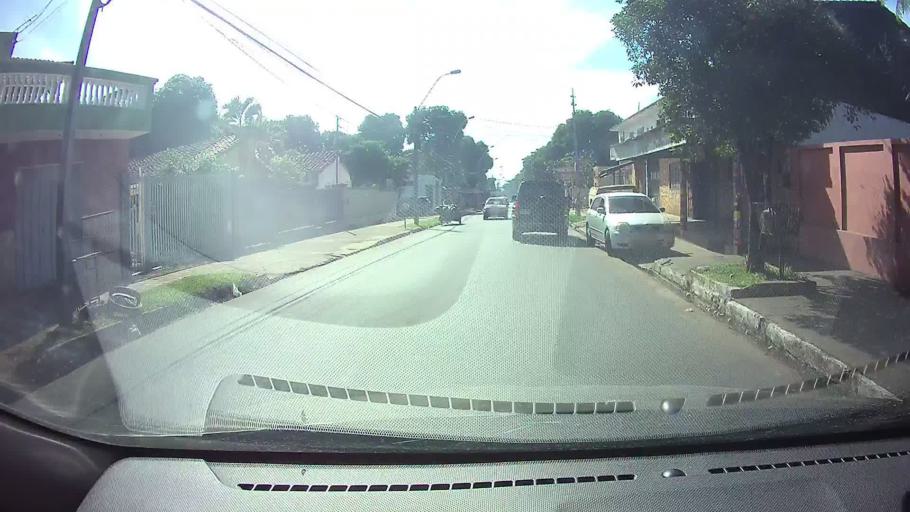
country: PY
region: Central
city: Fernando de la Mora
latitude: -25.3323
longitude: -57.5585
